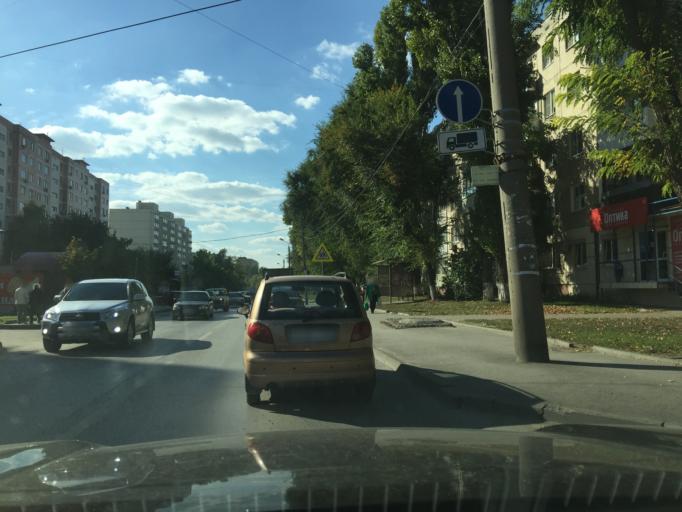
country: RU
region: Rostov
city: Rostov-na-Donu
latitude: 47.2037
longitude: 39.6322
